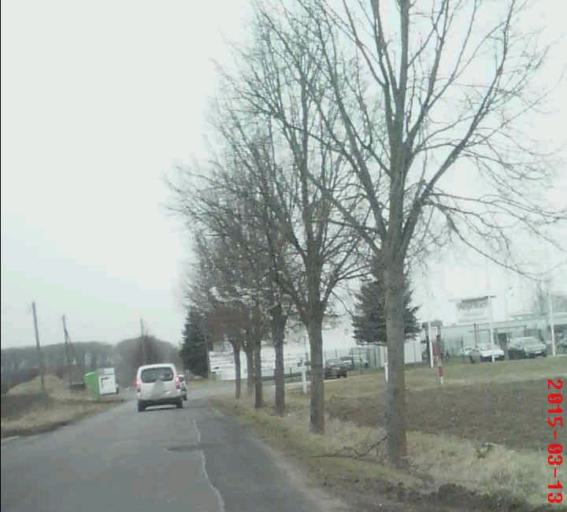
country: DE
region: Thuringia
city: Bad Langensalza
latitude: 51.1022
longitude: 10.6741
